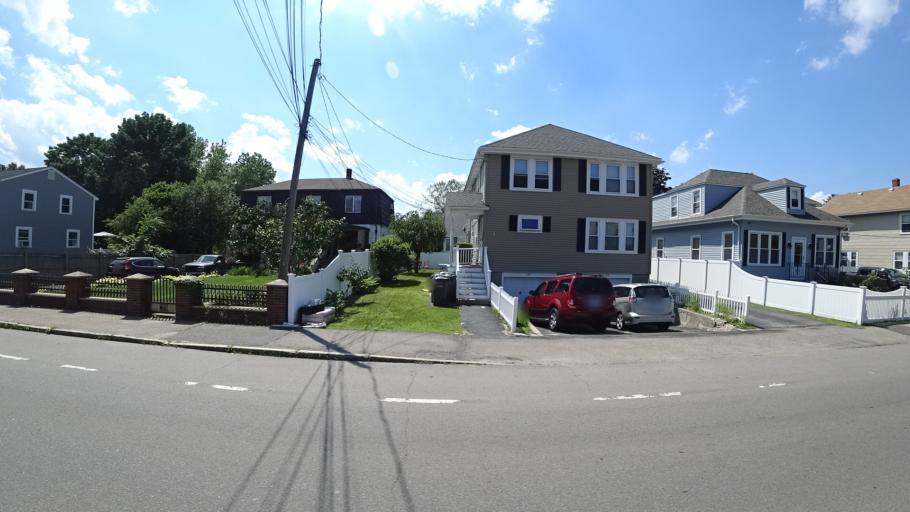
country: US
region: Massachusetts
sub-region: Norfolk County
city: Dedham
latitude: 42.2620
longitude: -71.1777
